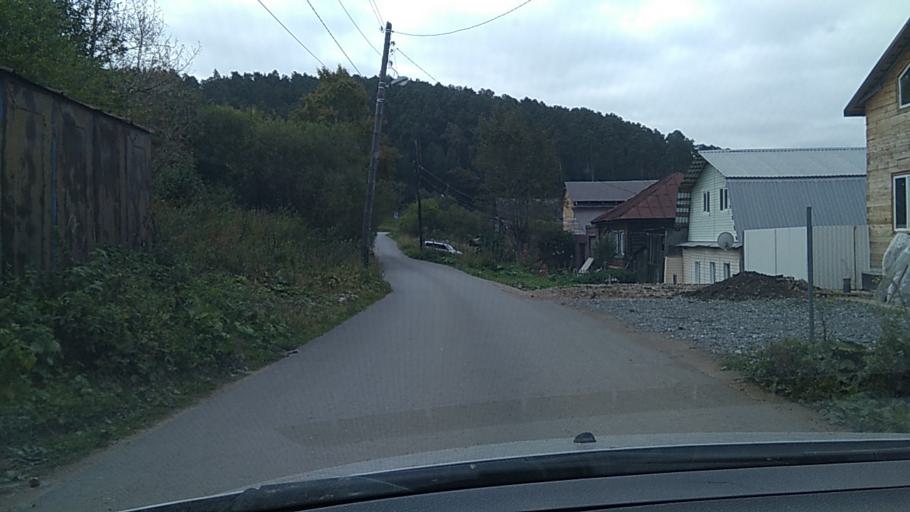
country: RU
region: Chelyabinsk
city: Zlatoust
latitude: 55.1720
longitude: 59.7108
